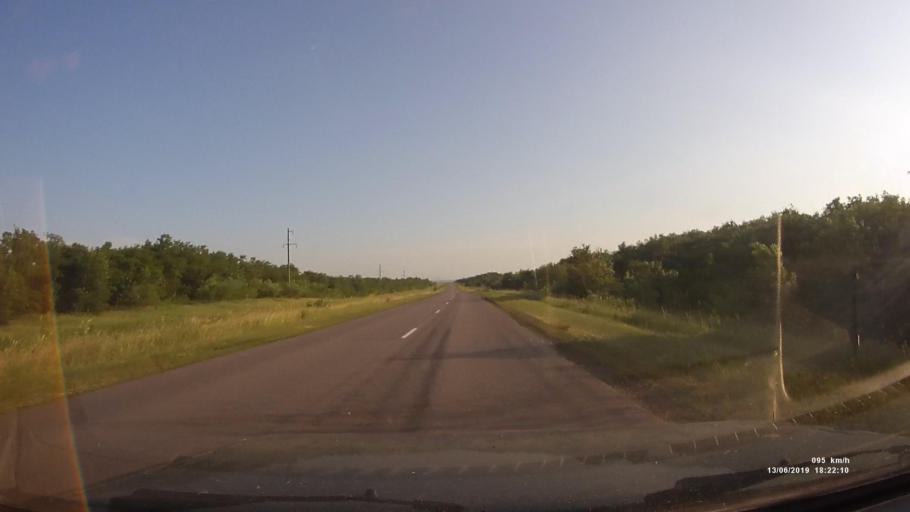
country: RU
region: Rostov
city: Kazanskaya
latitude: 49.8620
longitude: 41.2812
